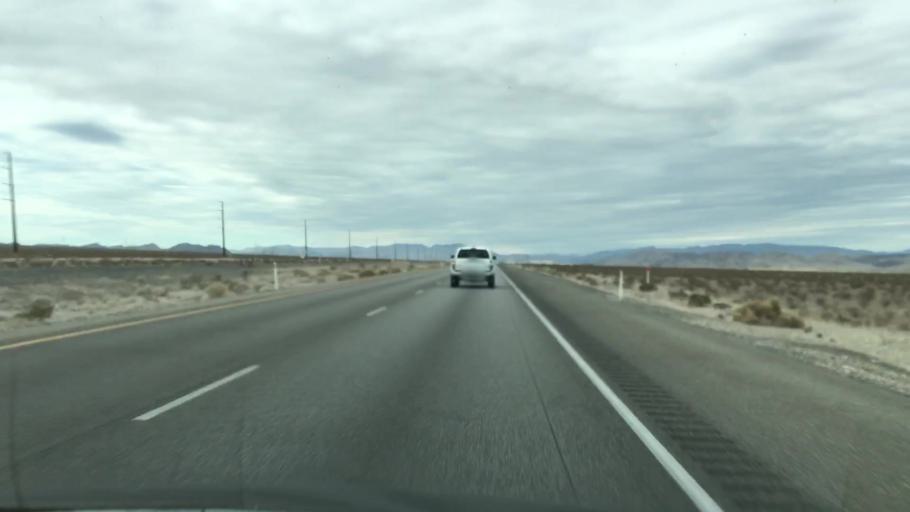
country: US
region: Nevada
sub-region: Clark County
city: Summerlin South
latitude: 36.5248
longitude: -115.5496
